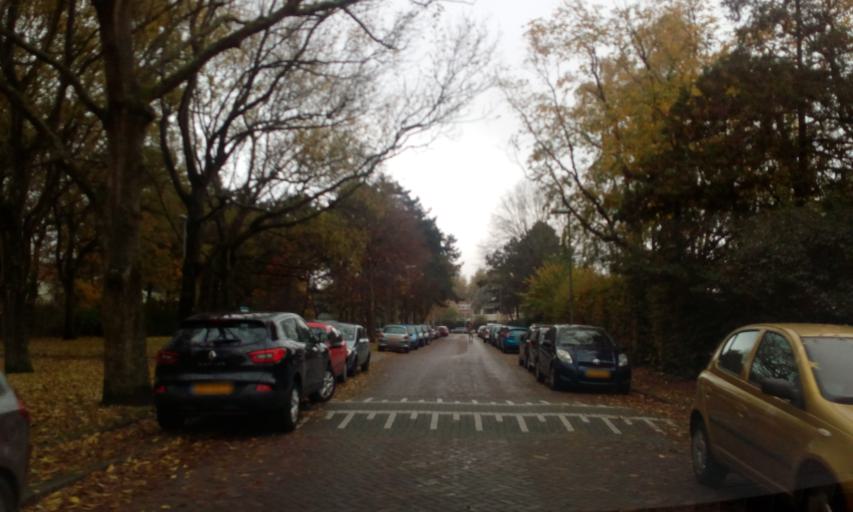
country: NL
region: South Holland
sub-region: Gemeente Lansingerland
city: Bergschenhoek
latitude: 51.9582
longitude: 4.5127
